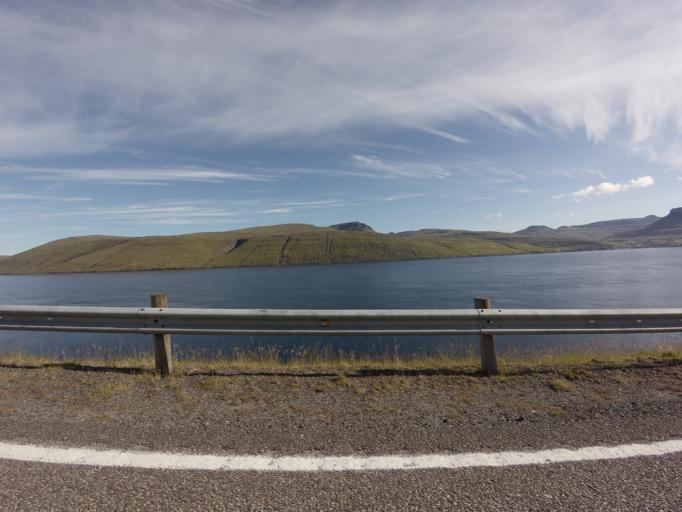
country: FO
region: Streymoy
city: Vestmanna
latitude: 62.0998
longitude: -7.1202
